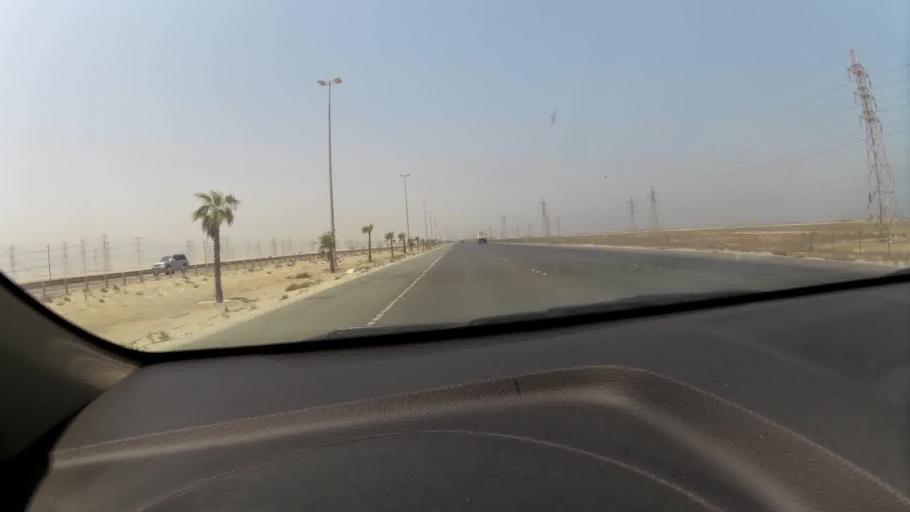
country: KW
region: Al Ahmadi
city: Al Fahahil
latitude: 28.8276
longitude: 48.2565
